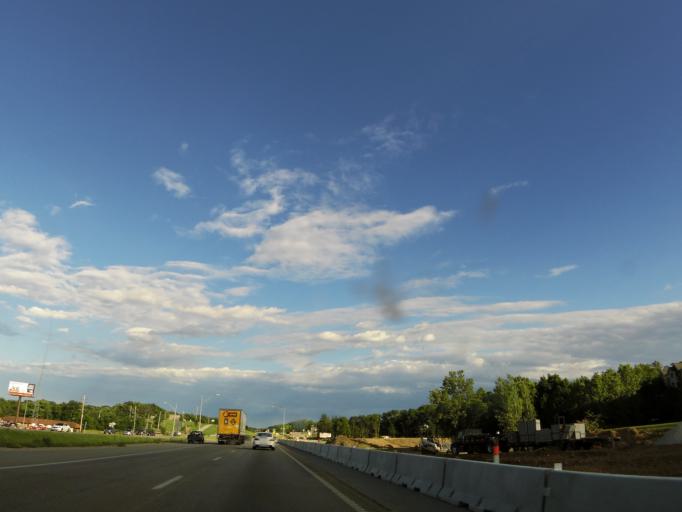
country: US
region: Missouri
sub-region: Saint Charles County
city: Wentzville
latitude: 38.8532
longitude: -90.8703
